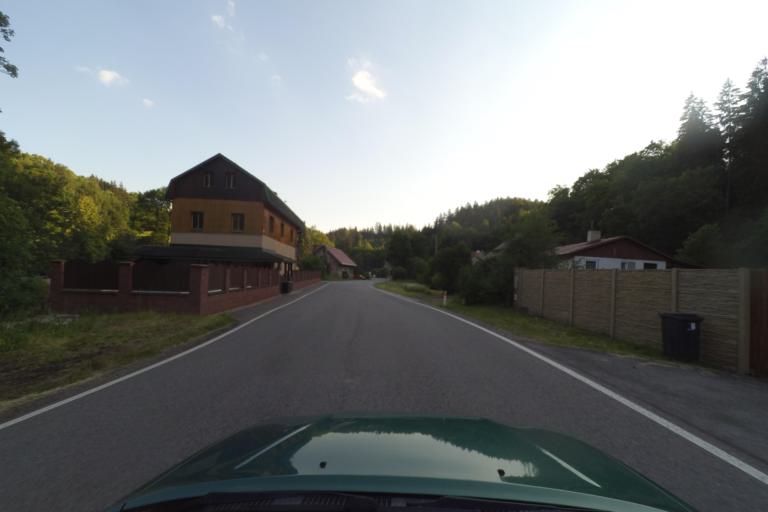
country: CZ
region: Kralovehradecky
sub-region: Okres Trutnov
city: Hostinne
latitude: 50.5672
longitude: 15.7243
